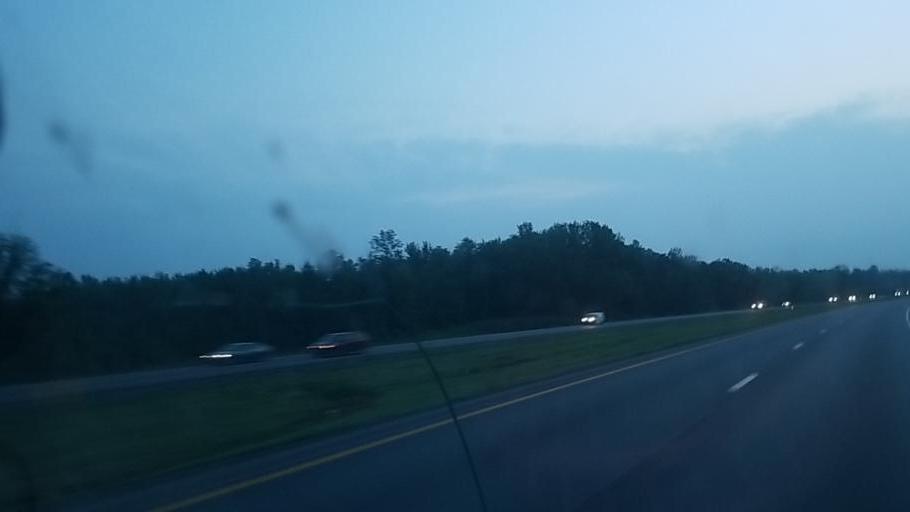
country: US
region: New York
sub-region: Madison County
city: Chittenango
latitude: 43.0941
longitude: -75.8289
